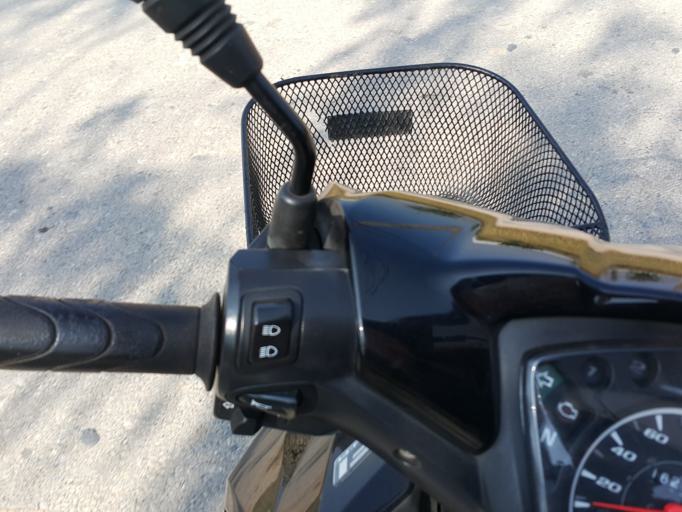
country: TH
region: Lamphun
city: Ban Thi
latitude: 18.6390
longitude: 99.0644
